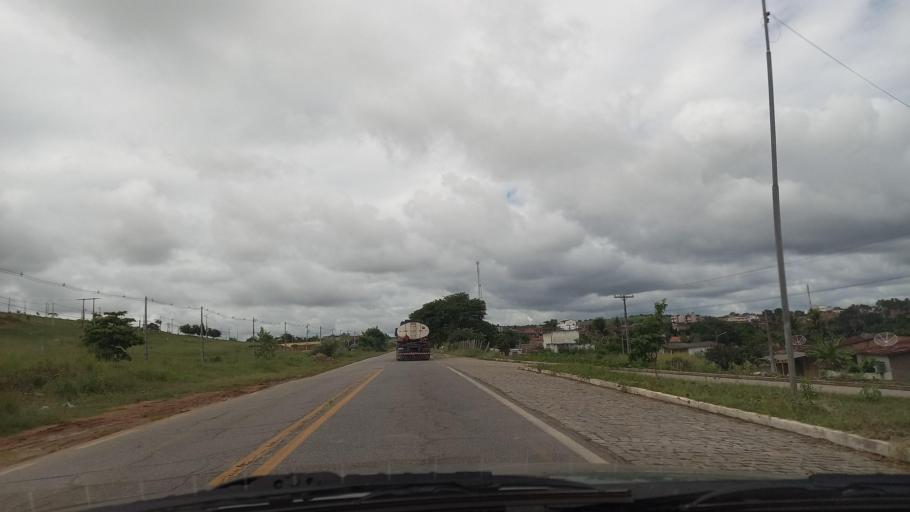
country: BR
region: Pernambuco
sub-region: Canhotinho
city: Canhotinho
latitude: -8.8754
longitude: -36.2059
